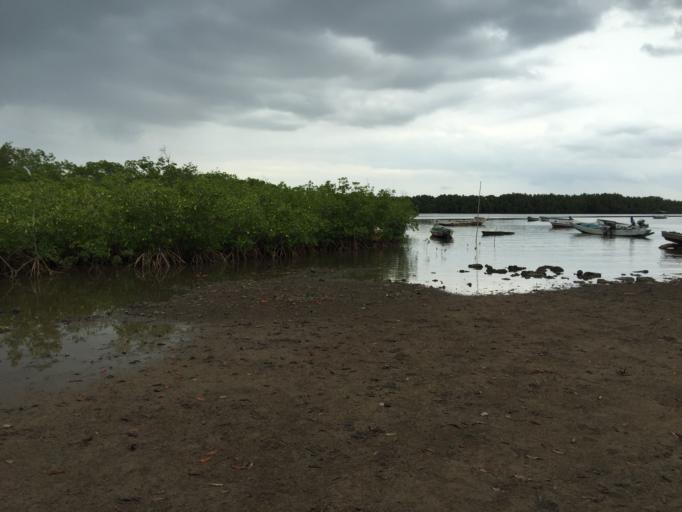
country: SN
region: Fatick
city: Sokone
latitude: 13.7853
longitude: -16.4789
